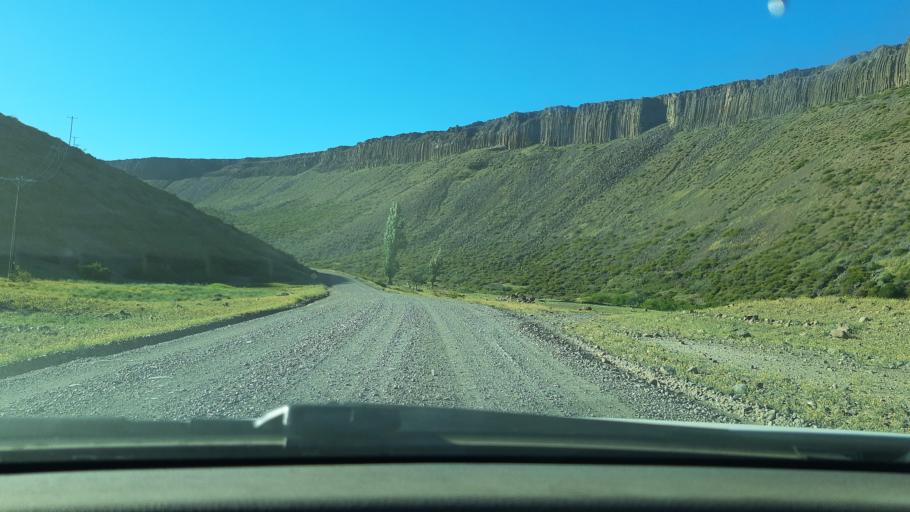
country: AR
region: Neuquen
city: Las Ovejas
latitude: -36.8192
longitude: -70.6993
